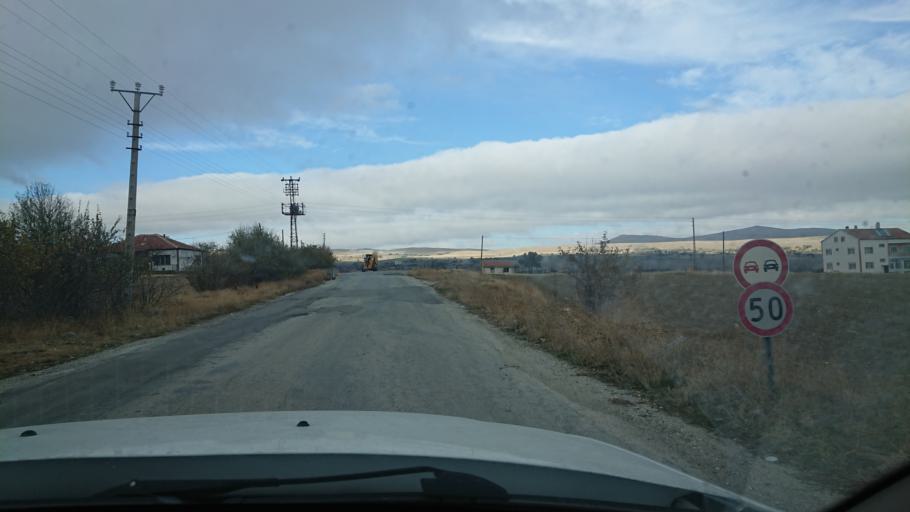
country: TR
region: Aksaray
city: Ortakoy
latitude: 38.7463
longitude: 34.0295
